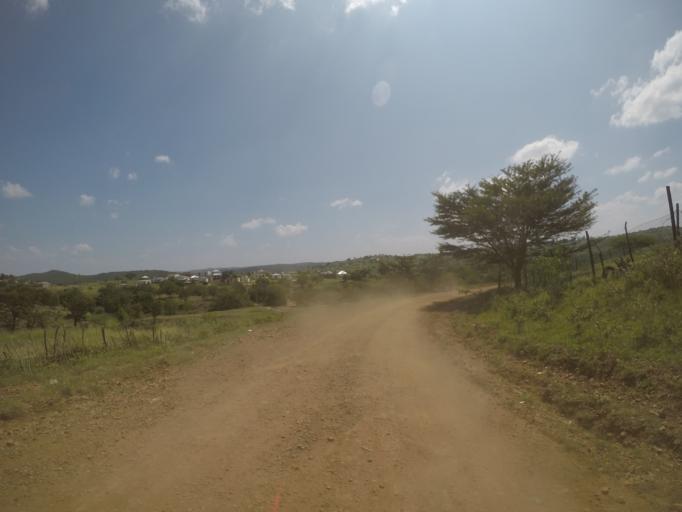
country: ZA
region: KwaZulu-Natal
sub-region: uThungulu District Municipality
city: Empangeni
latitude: -28.5941
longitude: 31.7365
